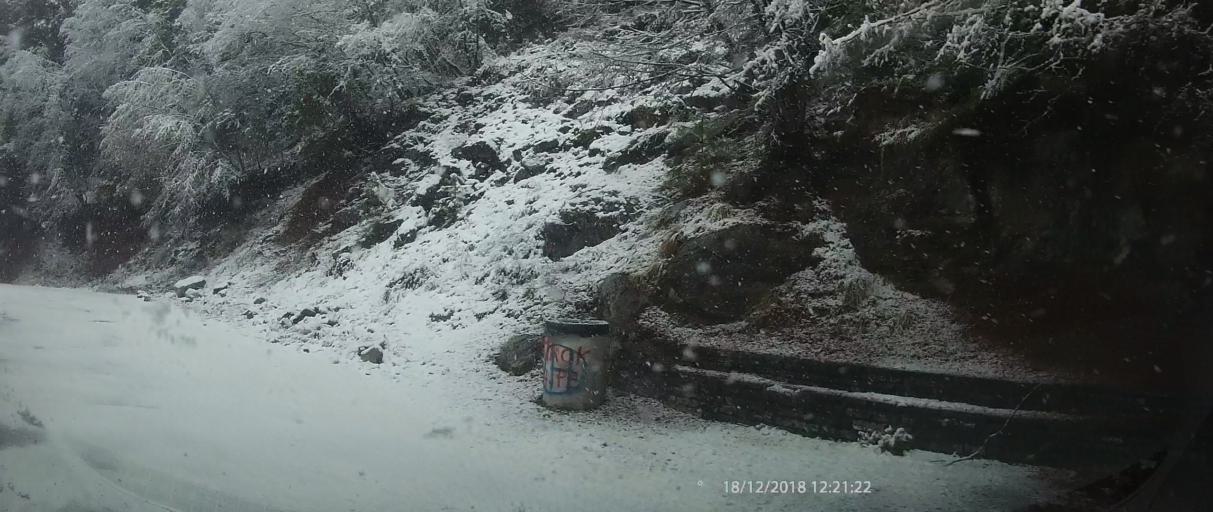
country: GR
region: Central Macedonia
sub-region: Nomos Pierias
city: Litochoro
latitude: 40.0957
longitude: 22.4206
